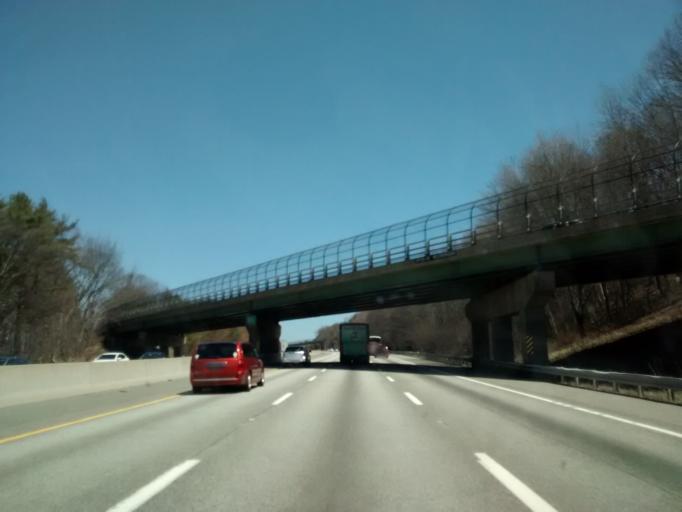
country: US
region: Massachusetts
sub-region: Worcester County
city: Westborough
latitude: 42.2355
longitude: -71.6049
